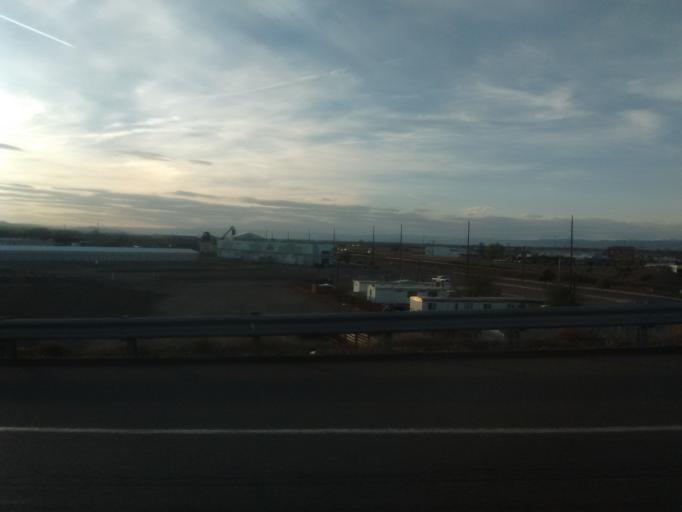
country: US
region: Colorado
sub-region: Mesa County
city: Redlands
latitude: 39.0904
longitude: -108.6101
